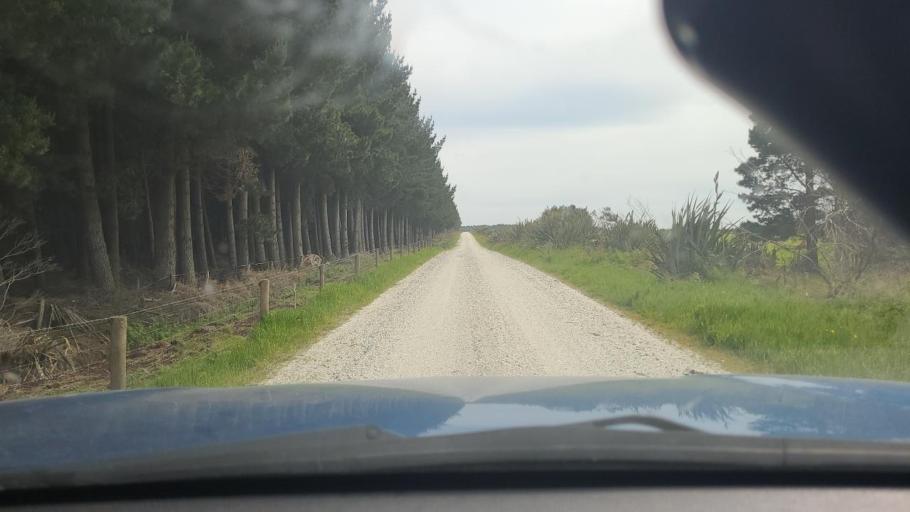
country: NZ
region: Southland
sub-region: Invercargill City
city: Bluff
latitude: -46.5457
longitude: 168.6172
